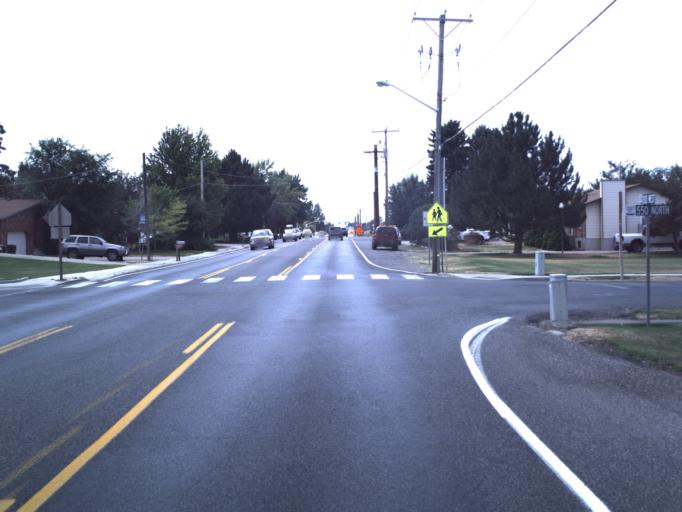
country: US
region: Utah
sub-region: Davis County
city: West Point
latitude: 41.1219
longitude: -112.0646
